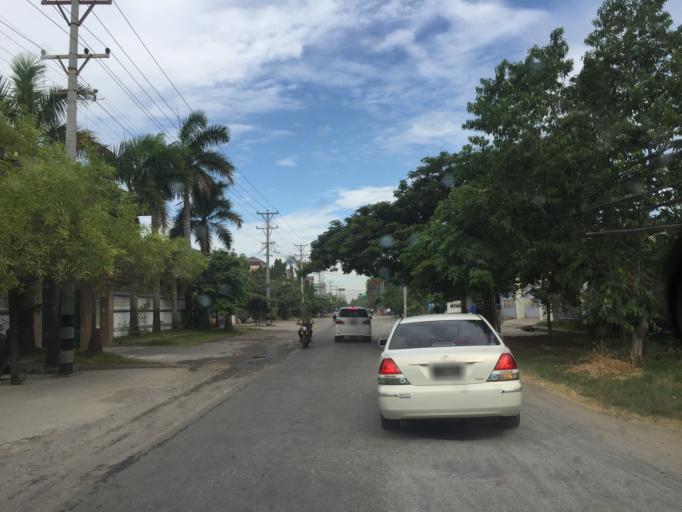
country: MM
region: Mandalay
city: Mandalay
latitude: 21.9726
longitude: 96.1075
